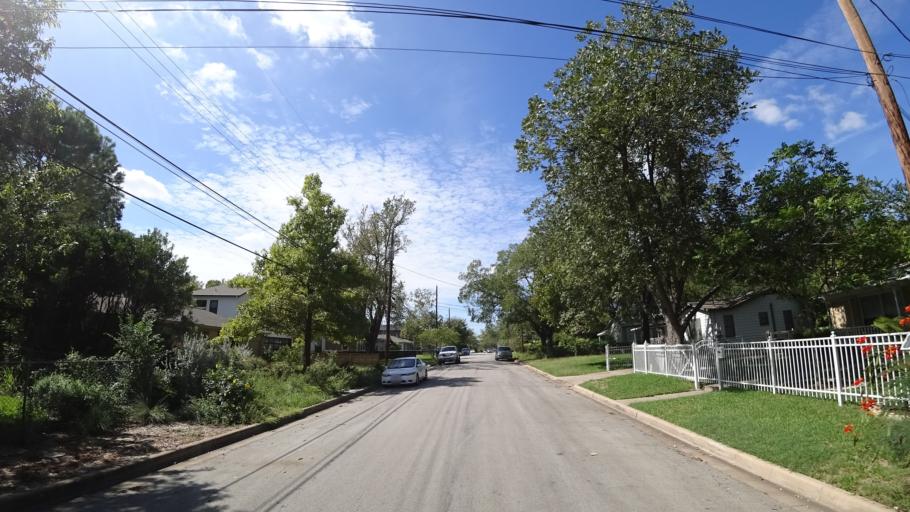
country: US
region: Texas
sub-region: Travis County
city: Austin
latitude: 30.3431
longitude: -97.7230
